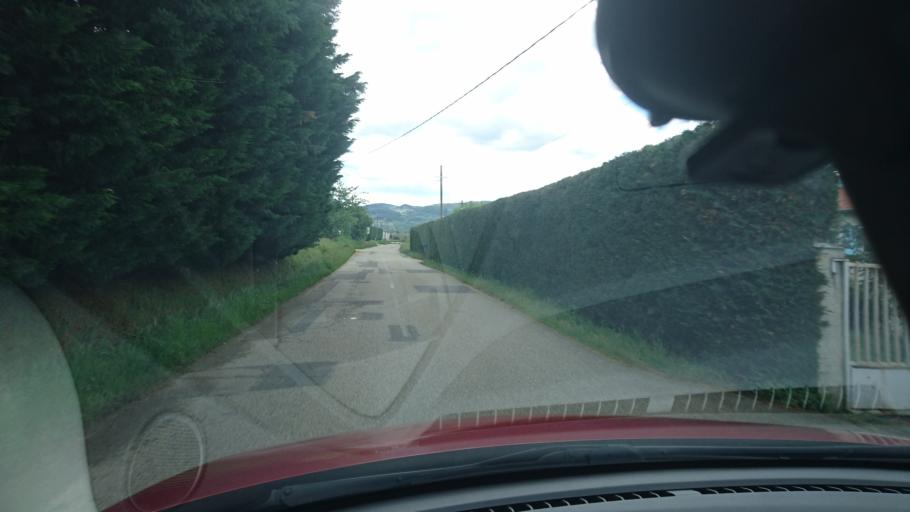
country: FR
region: Rhone-Alpes
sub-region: Departement de la Loire
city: Maclas
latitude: 45.3575
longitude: 4.6985
